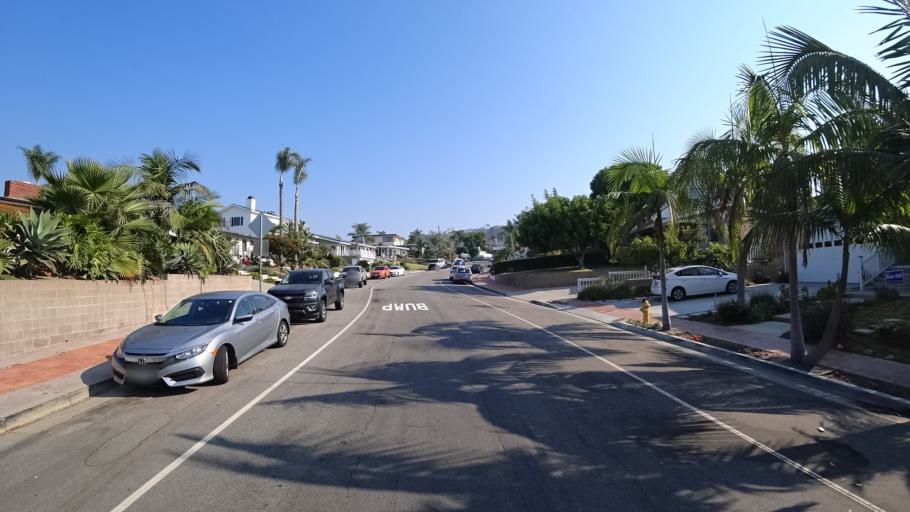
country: US
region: California
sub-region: Orange County
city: San Clemente
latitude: 33.4179
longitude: -117.6117
